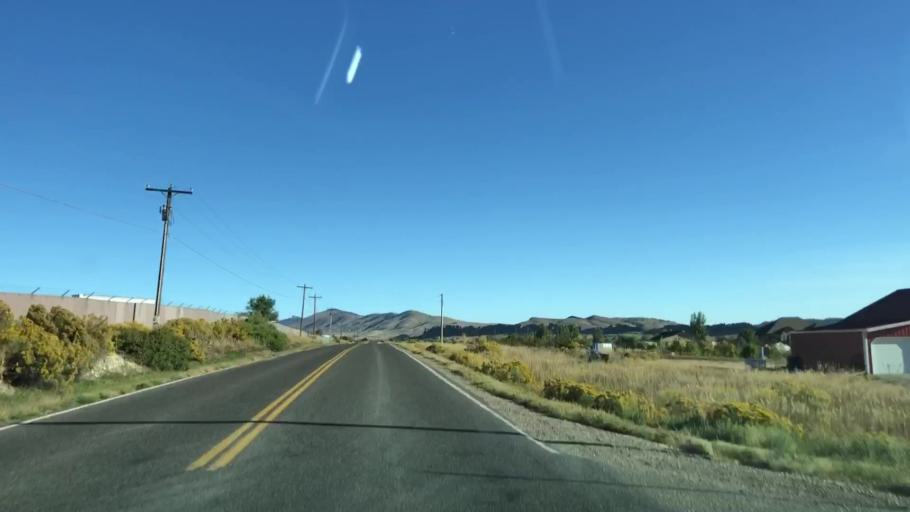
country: US
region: Colorado
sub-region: Larimer County
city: Loveland
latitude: 40.3943
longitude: -105.1681
